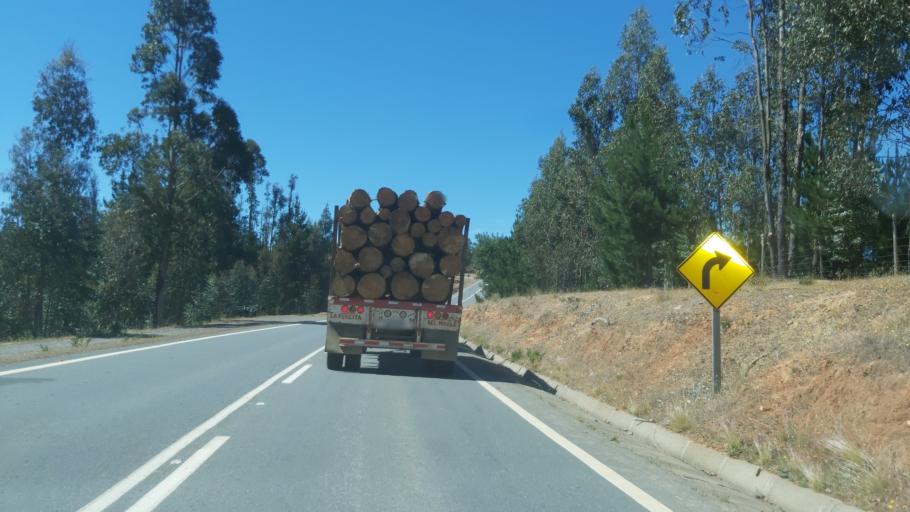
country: CL
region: Maule
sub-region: Provincia de Talca
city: Constitucion
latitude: -34.9384
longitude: -71.9803
